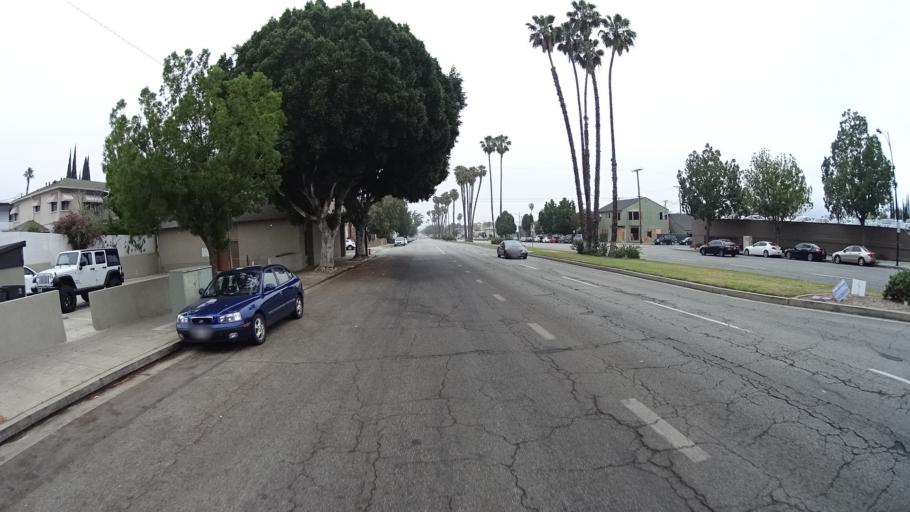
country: US
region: California
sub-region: Los Angeles County
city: Burbank
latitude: 34.1794
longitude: -118.3005
